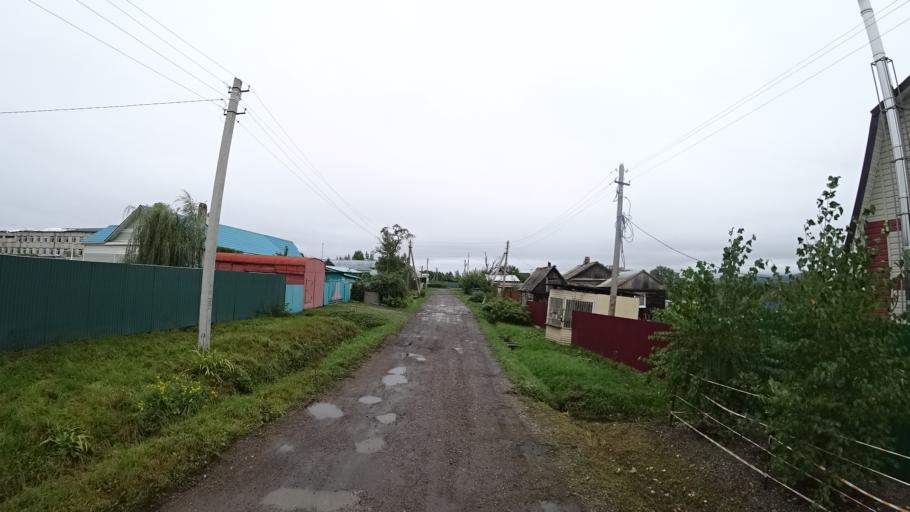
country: RU
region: Primorskiy
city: Monastyrishche
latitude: 44.2015
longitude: 132.4450
